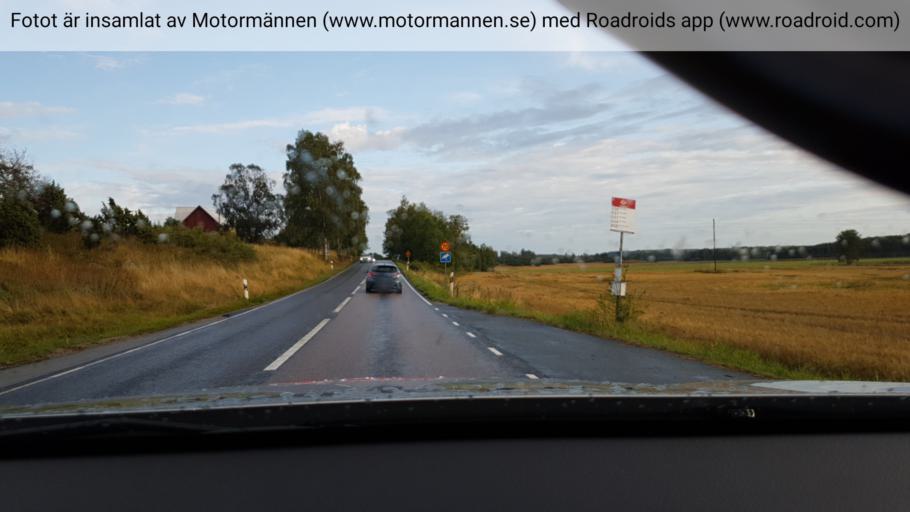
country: SE
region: Stockholm
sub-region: Norrtalje Kommun
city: Norrtalje
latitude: 59.7976
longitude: 18.6576
